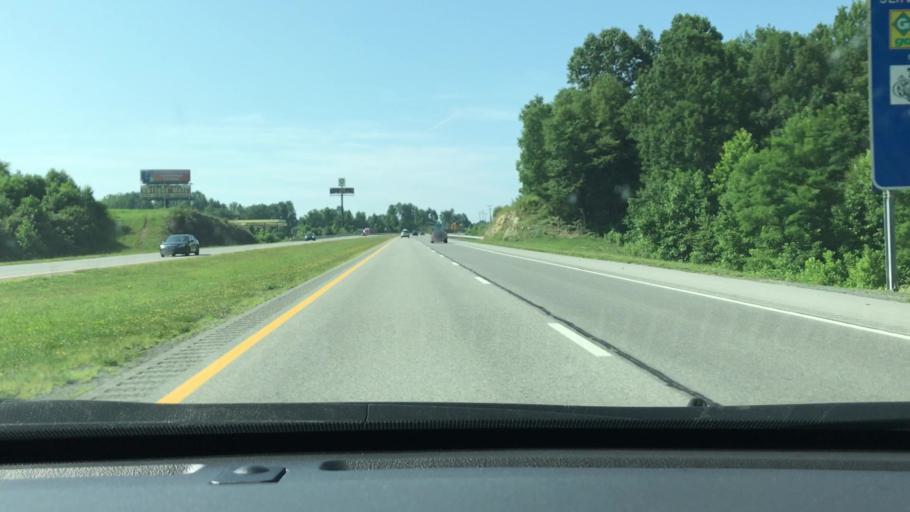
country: US
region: West Virginia
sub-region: Nicholas County
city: Summersville
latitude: 38.2159
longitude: -80.8513
